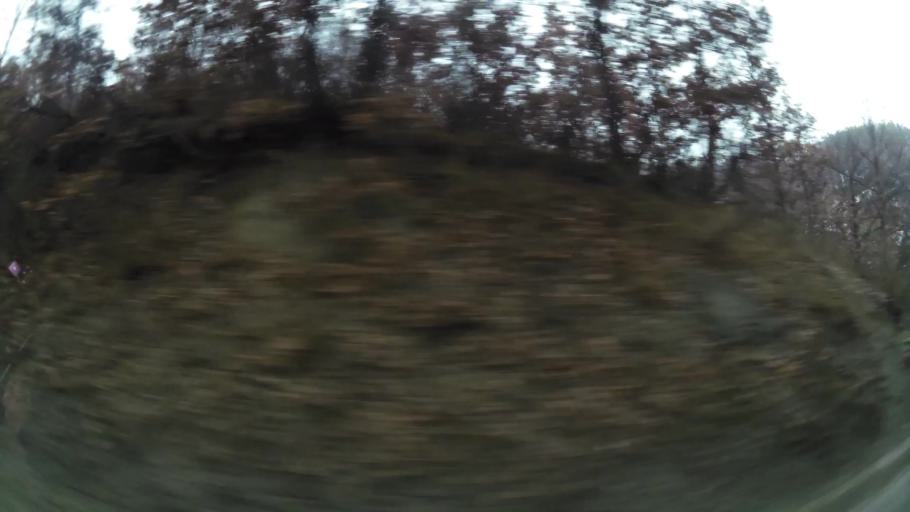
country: XK
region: Ferizaj
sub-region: Hani i Elezit
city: Hani i Elezit
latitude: 42.1729
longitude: 21.2744
